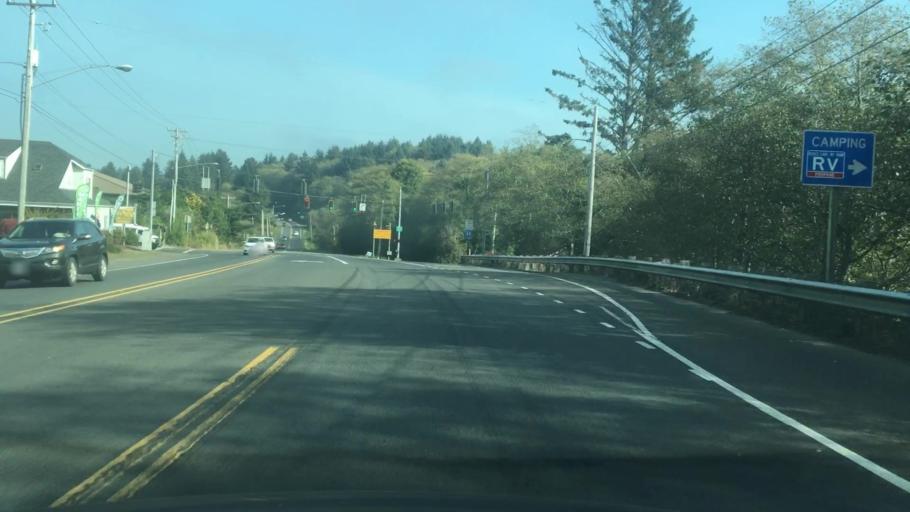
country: US
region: Oregon
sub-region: Lincoln County
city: Lincoln City
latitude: 44.9974
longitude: -123.9978
